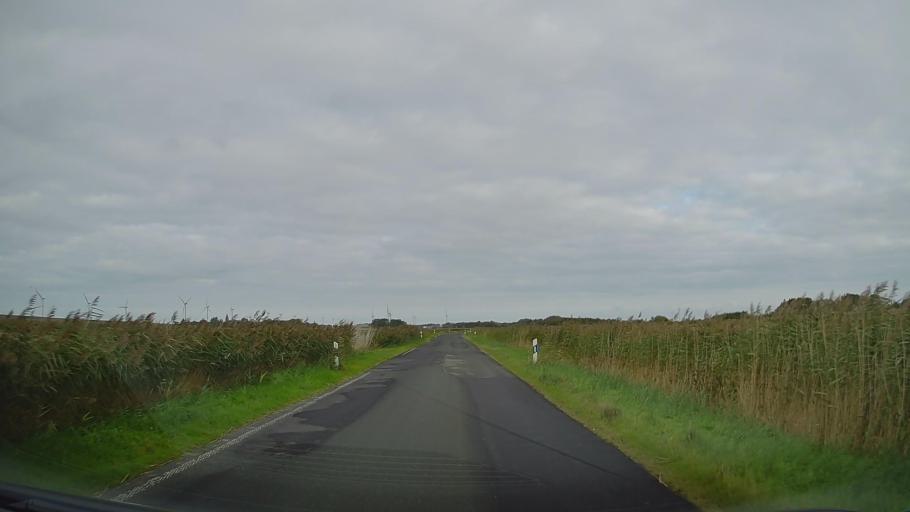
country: DE
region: Schleswig-Holstein
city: Emmelsbull-Horsbull
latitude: 54.8201
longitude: 8.6527
